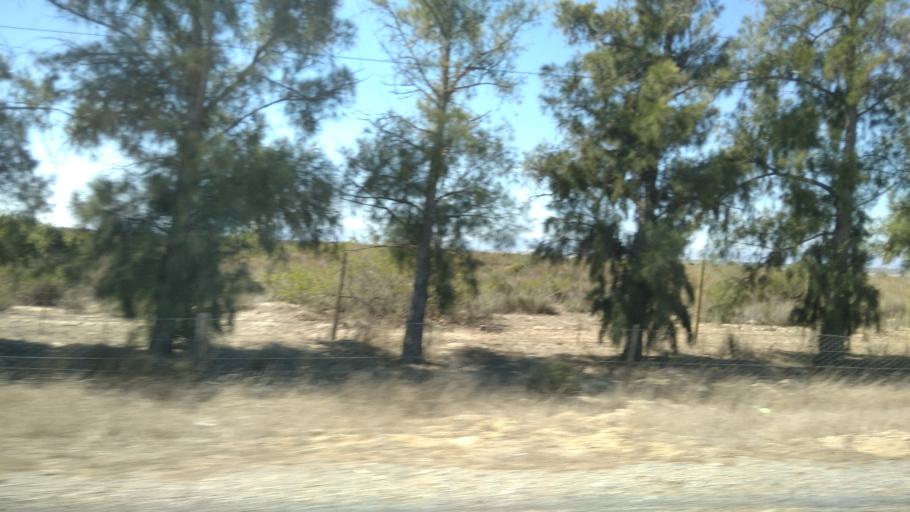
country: ZA
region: Western Cape
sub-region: West Coast District Municipality
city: Moorreesburg
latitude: -33.0471
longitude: 18.3242
